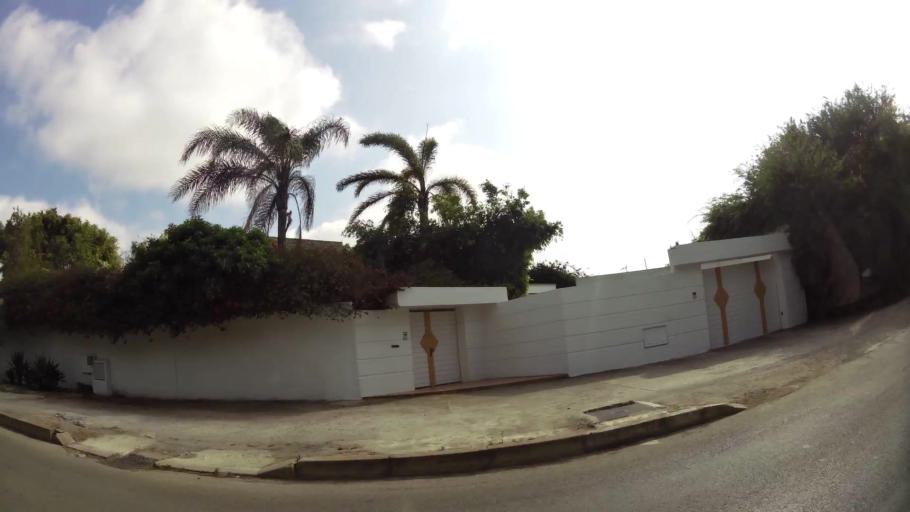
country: MA
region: Rabat-Sale-Zemmour-Zaer
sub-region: Rabat
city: Rabat
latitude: 33.9727
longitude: -6.8604
